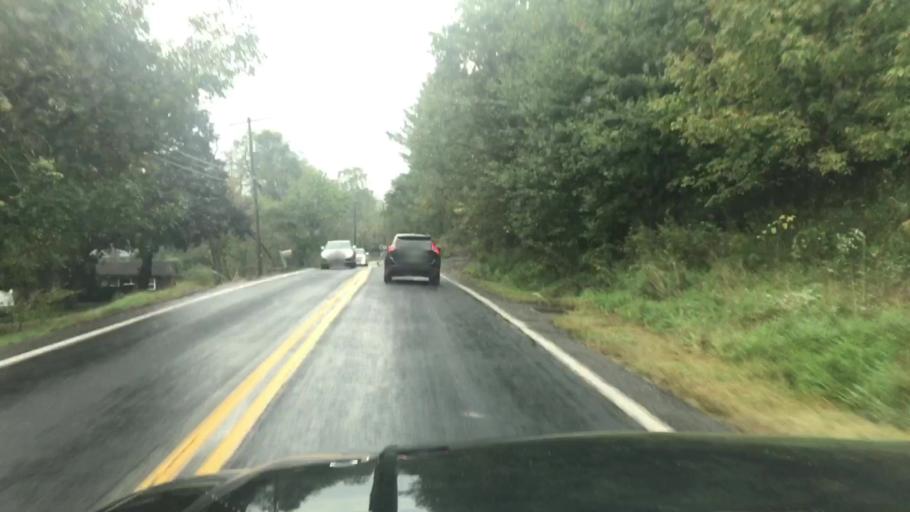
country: US
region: Pennsylvania
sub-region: Cumberland County
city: Shiremanstown
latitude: 40.1830
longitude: -76.9293
